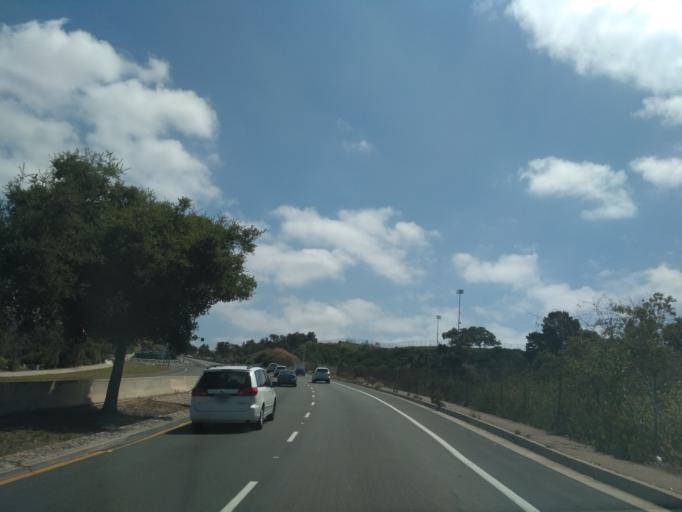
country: US
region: California
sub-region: San Diego County
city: La Jolla
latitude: 32.8081
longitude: -117.2096
